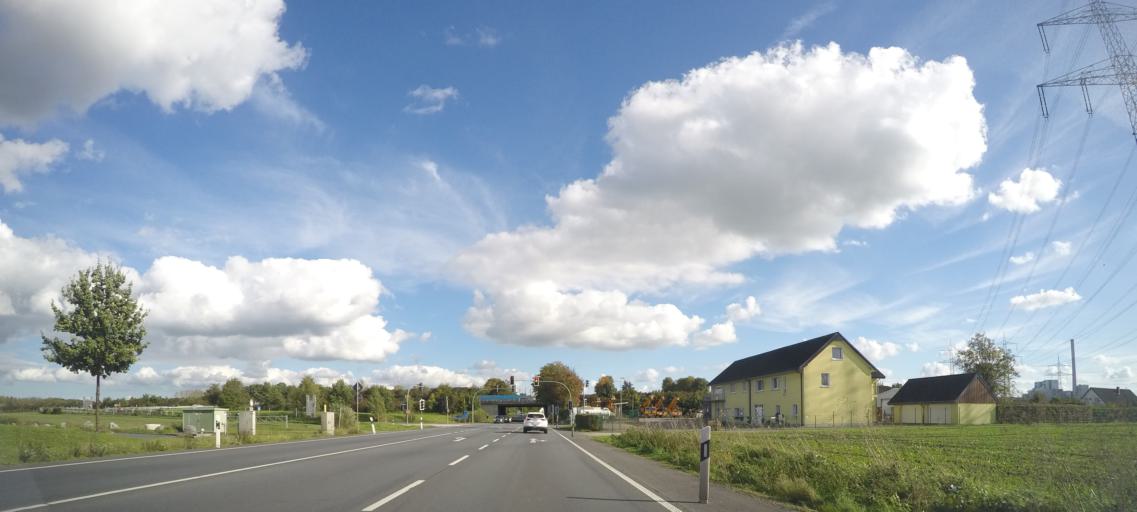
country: DE
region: North Rhine-Westphalia
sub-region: Regierungsbezirk Arnsberg
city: Welver
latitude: 51.6953
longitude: 7.9671
